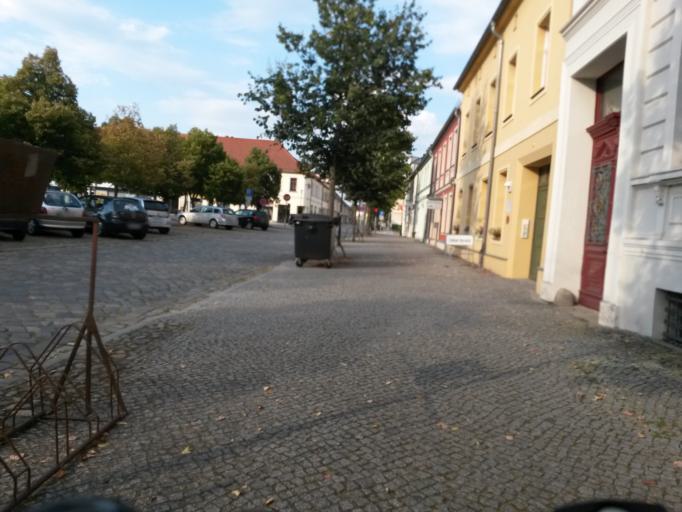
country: DE
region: Brandenburg
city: Templin
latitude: 53.1188
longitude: 13.5011
